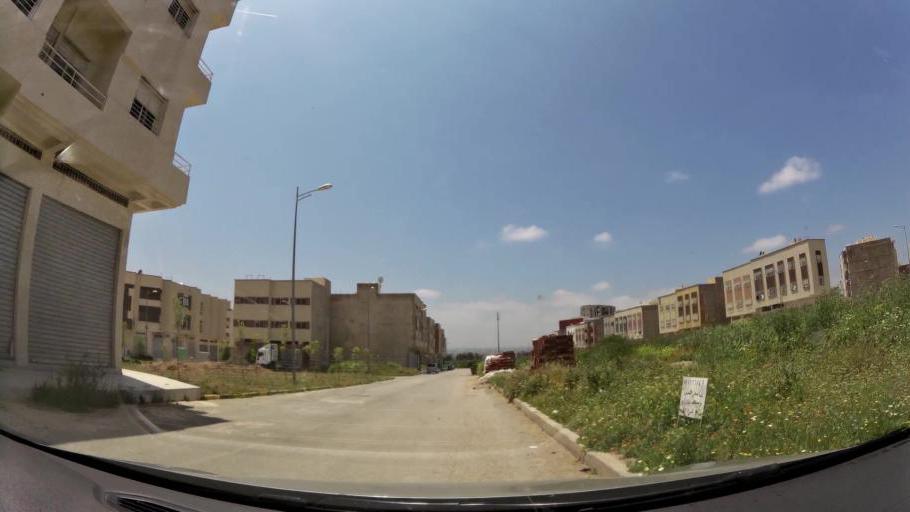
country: MA
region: Fes-Boulemane
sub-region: Fes
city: Fes
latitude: 34.0534
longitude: -5.0434
